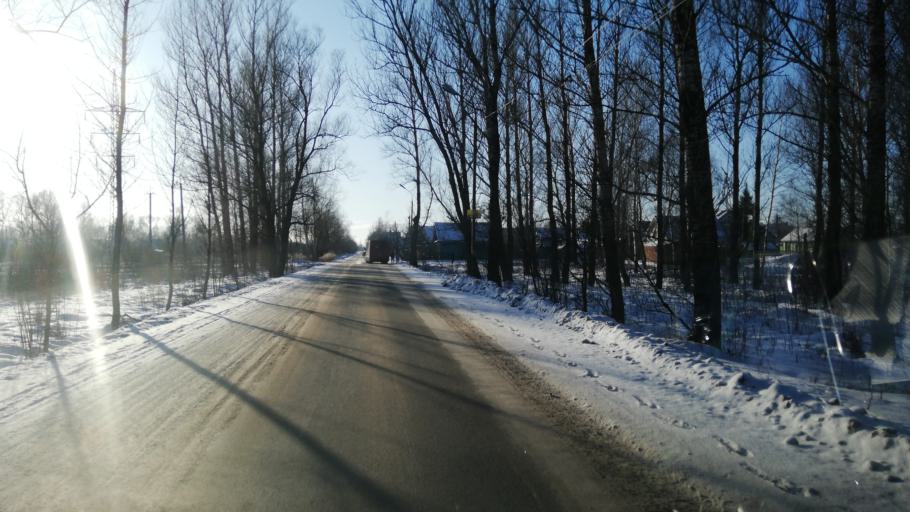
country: RU
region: Jaroslavl
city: Yaroslavl
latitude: 57.6197
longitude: 39.8090
